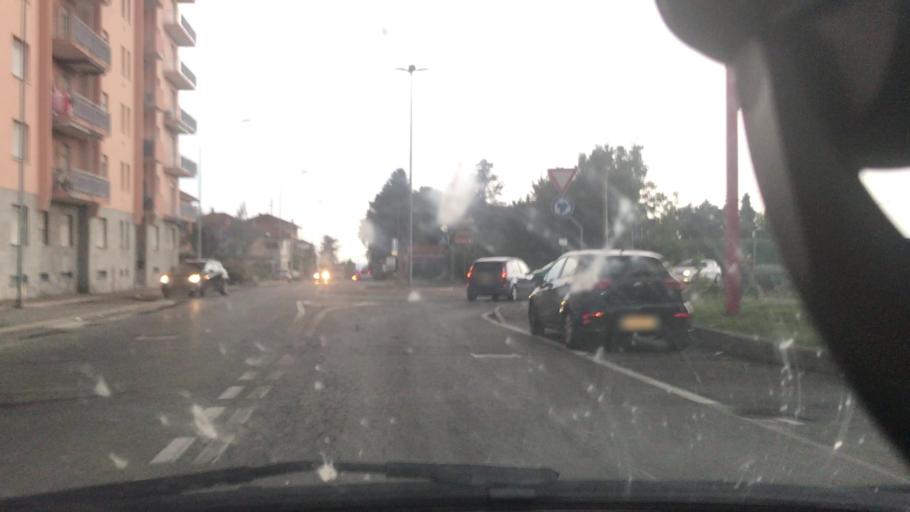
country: IT
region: Piedmont
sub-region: Provincia di Biella
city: Biella
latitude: 45.5693
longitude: 8.0722
